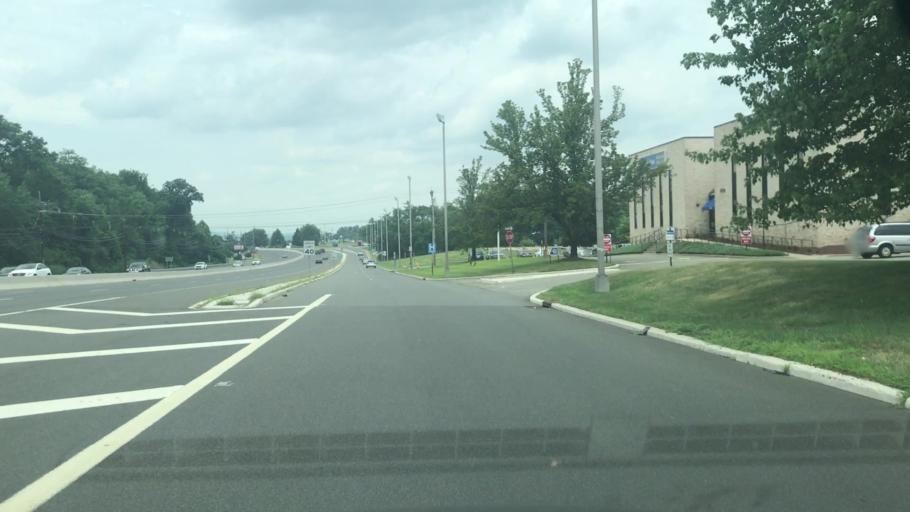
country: US
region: New Jersey
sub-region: Passaic County
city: Wayne
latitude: 40.9423
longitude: -74.2712
